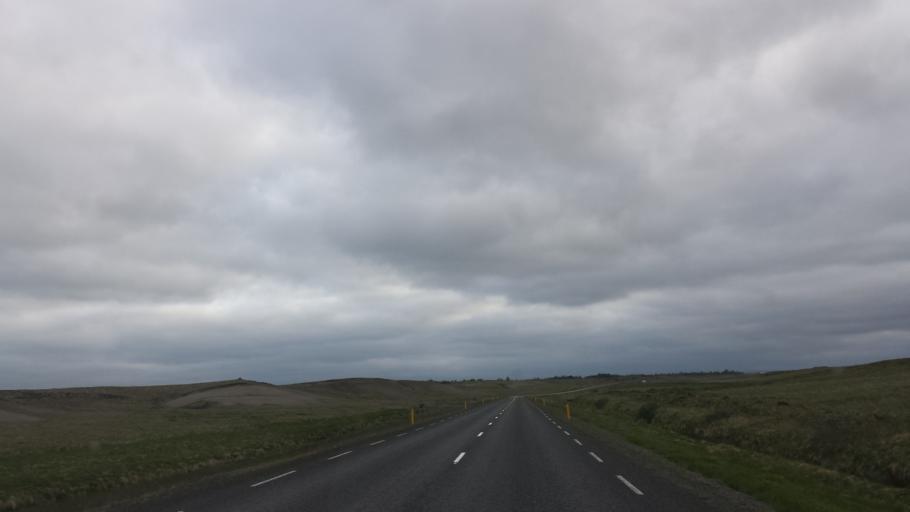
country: IS
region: South
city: Selfoss
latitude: 64.1275
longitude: -20.5895
